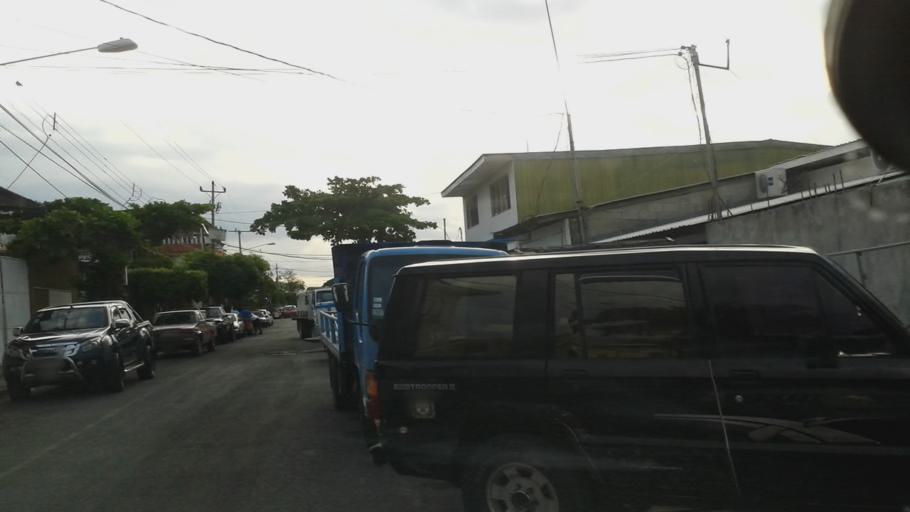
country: CR
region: Puntarenas
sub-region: Canton Central de Puntarenas
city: Puntarenas
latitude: 9.9776
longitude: -84.8471
